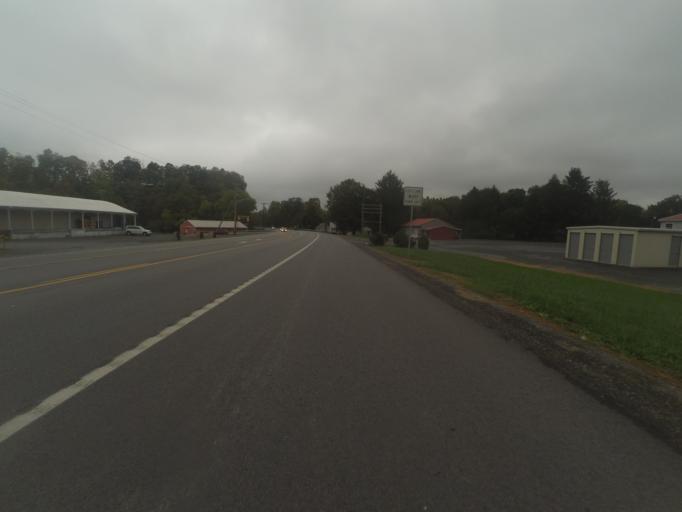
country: US
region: Pennsylvania
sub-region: Huntingdon County
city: McConnellstown
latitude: 40.5376
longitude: -78.0865
